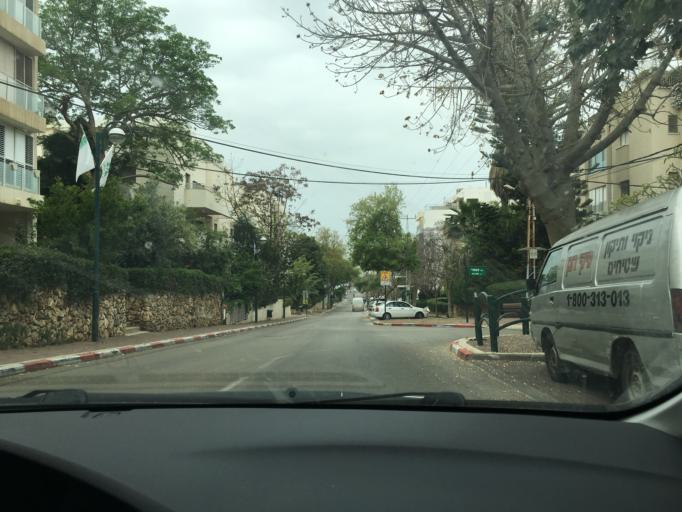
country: IL
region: Tel Aviv
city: Ramat HaSharon
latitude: 32.1419
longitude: 34.8406
